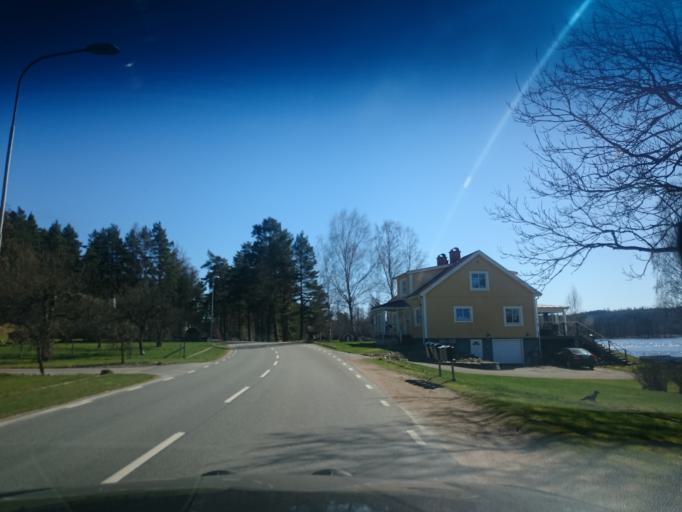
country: SE
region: Kronoberg
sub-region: Vaxjo Kommun
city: Braas
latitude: 57.2017
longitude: 14.9563
